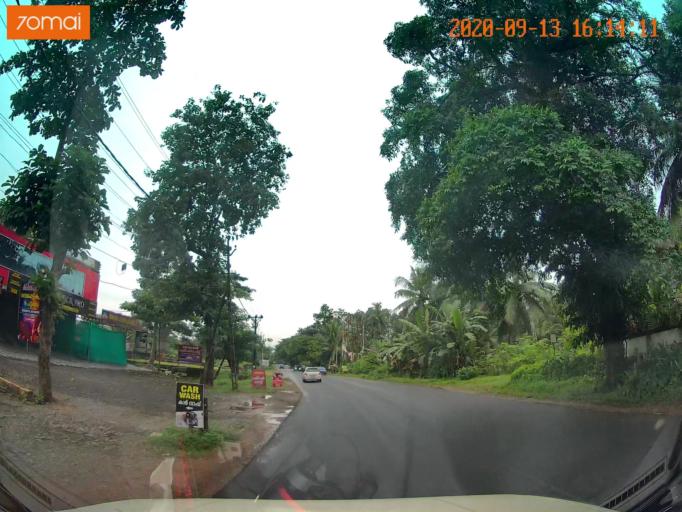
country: IN
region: Kerala
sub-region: Kottayam
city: Palackattumala
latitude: 9.6887
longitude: 76.6330
